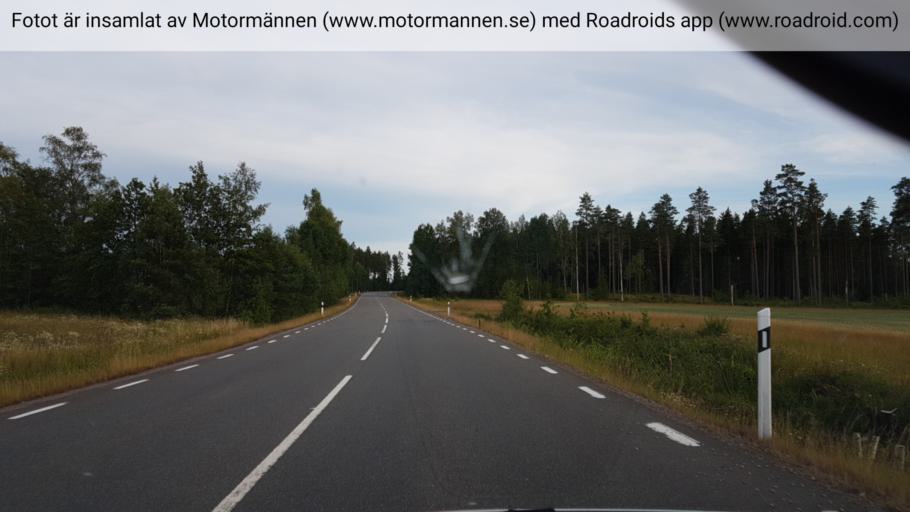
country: SE
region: Vaestra Goetaland
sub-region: Tibro Kommun
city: Tibro
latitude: 58.5125
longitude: 14.1619
